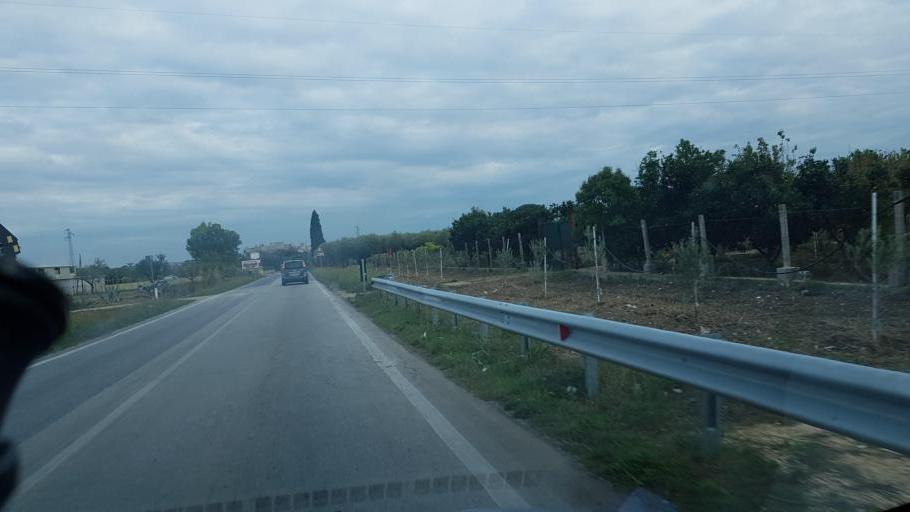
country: IT
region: Apulia
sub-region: Provincia di Brindisi
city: Oria
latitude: 40.5111
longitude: 17.6222
